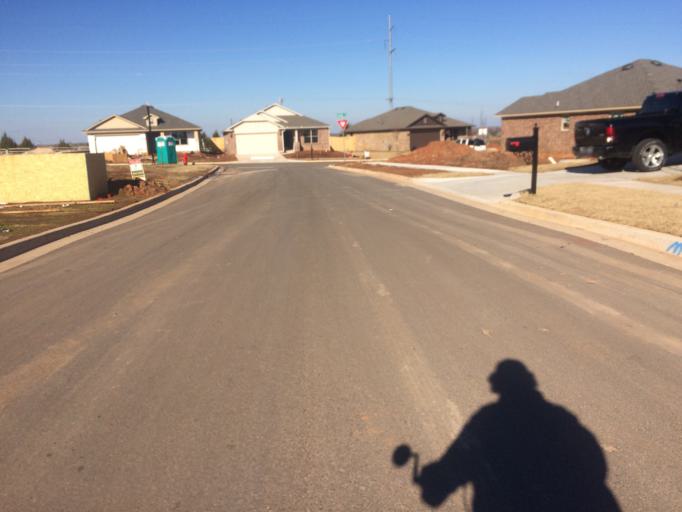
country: US
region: Oklahoma
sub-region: Cleveland County
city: Norman
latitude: 35.2535
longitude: -97.4557
